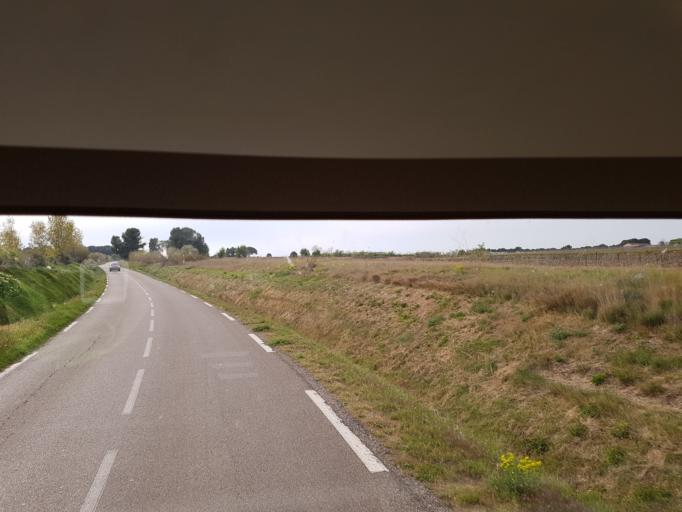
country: FR
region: Languedoc-Roussillon
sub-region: Departement de l'Herault
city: Marseillan
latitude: 43.3676
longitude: 3.5093
